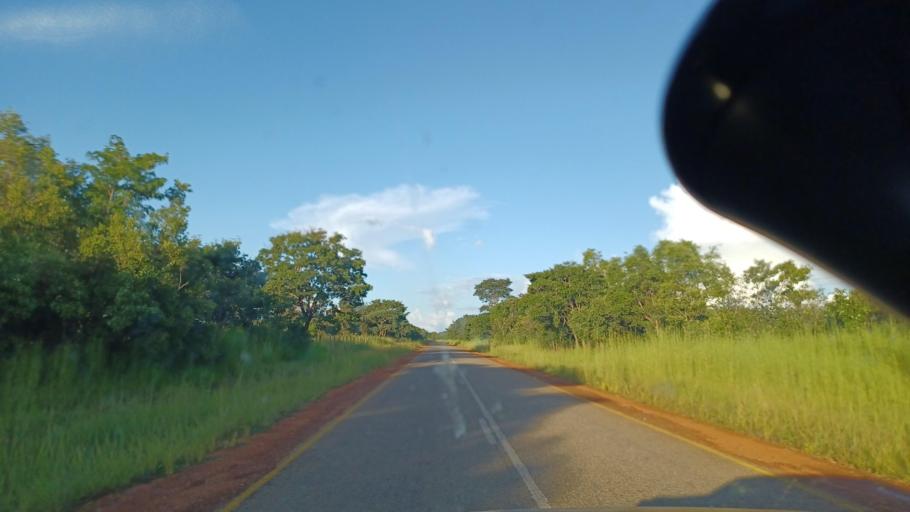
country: ZM
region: North-Western
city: Kalengwa
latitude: -13.1443
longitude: 25.0561
